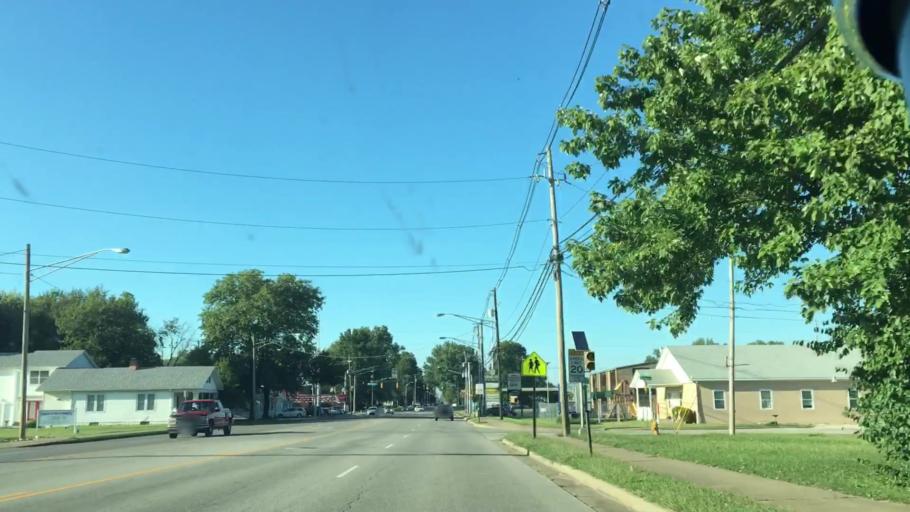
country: US
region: Indiana
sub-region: Vanderburgh County
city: Evansville
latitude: 37.9459
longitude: -87.4929
